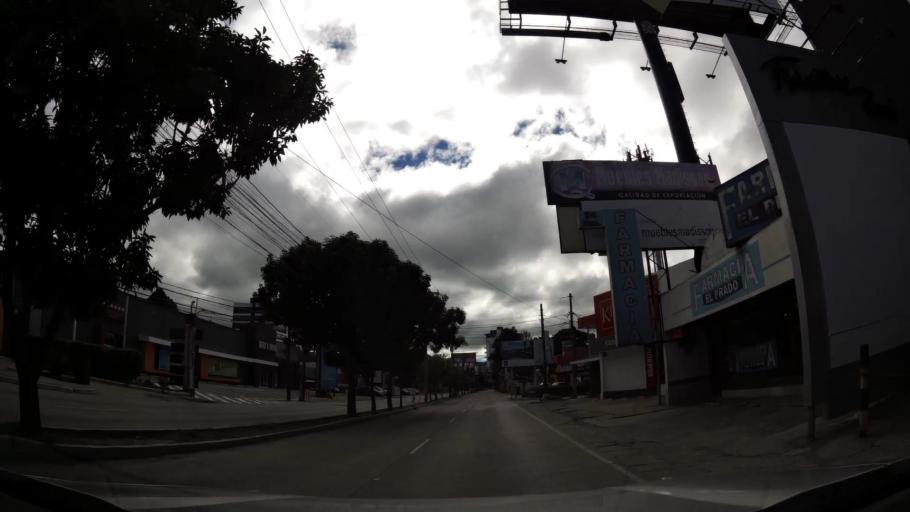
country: GT
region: Guatemala
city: Santa Catarina Pinula
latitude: 14.5958
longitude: -90.5067
